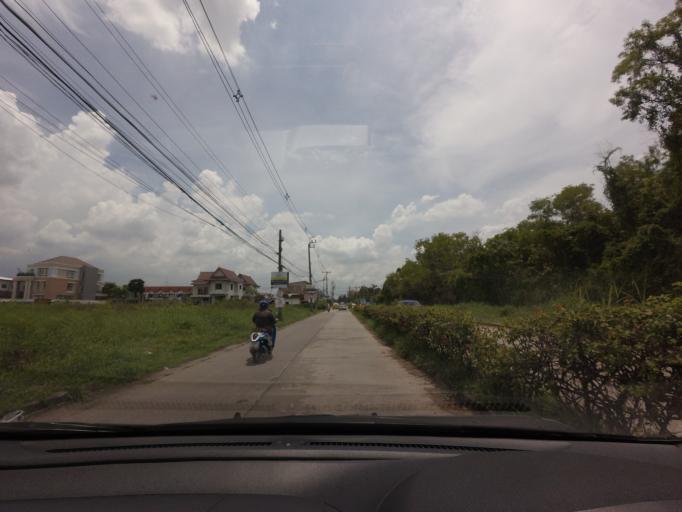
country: TH
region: Bangkok
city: Don Mueang
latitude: 13.9380
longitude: 100.5858
